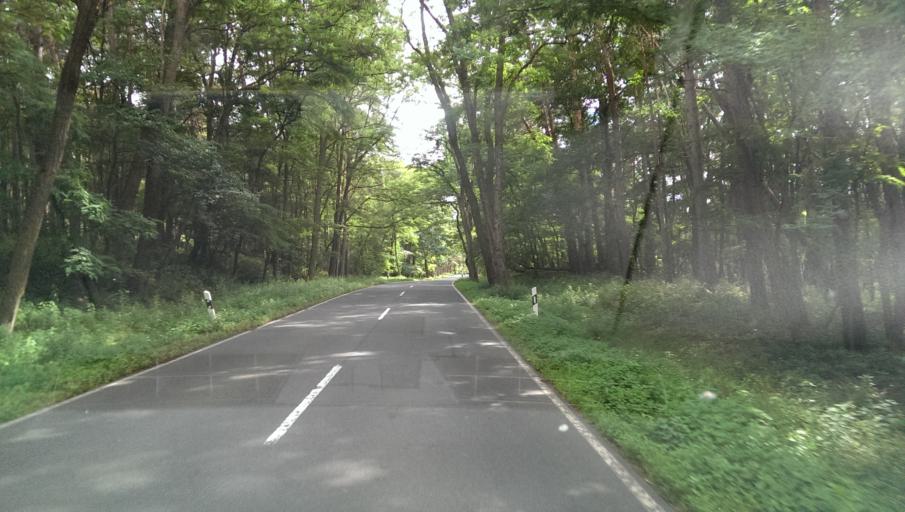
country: DE
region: Saxony-Anhalt
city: Nudersdorf
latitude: 51.9339
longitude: 12.5470
